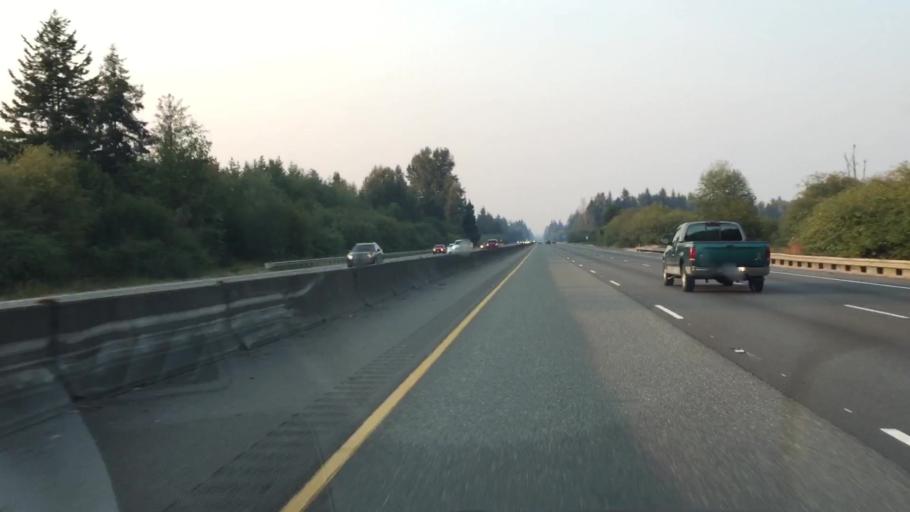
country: US
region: Washington
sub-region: Thurston County
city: Tumwater
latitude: 46.9251
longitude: -122.9456
